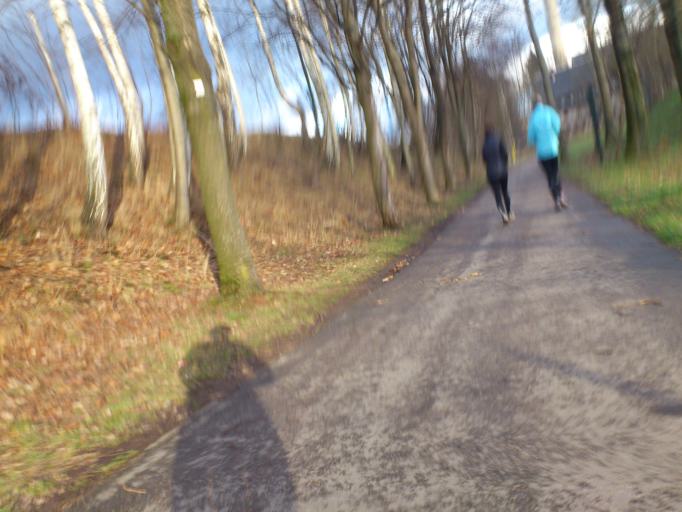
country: DE
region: Saxony
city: Chemnitz
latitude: 50.7966
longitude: 12.9105
